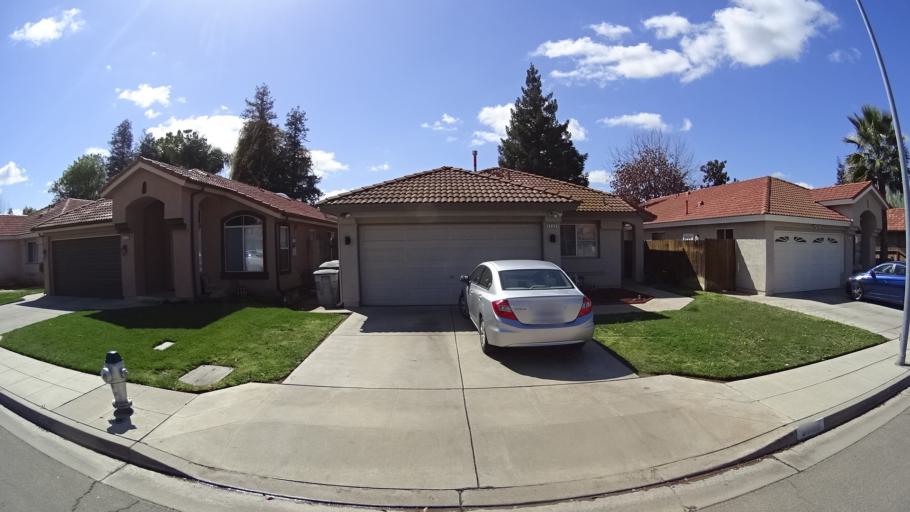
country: US
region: California
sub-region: Fresno County
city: Biola
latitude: 36.8272
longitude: -119.8942
